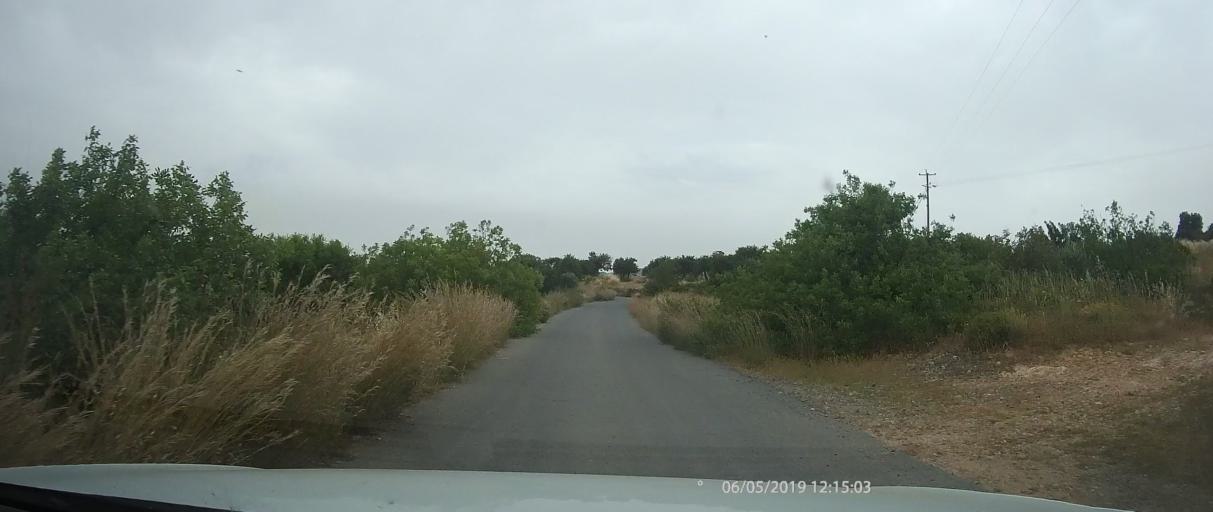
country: CY
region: Pafos
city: Tala
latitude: 34.8498
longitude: 32.4222
